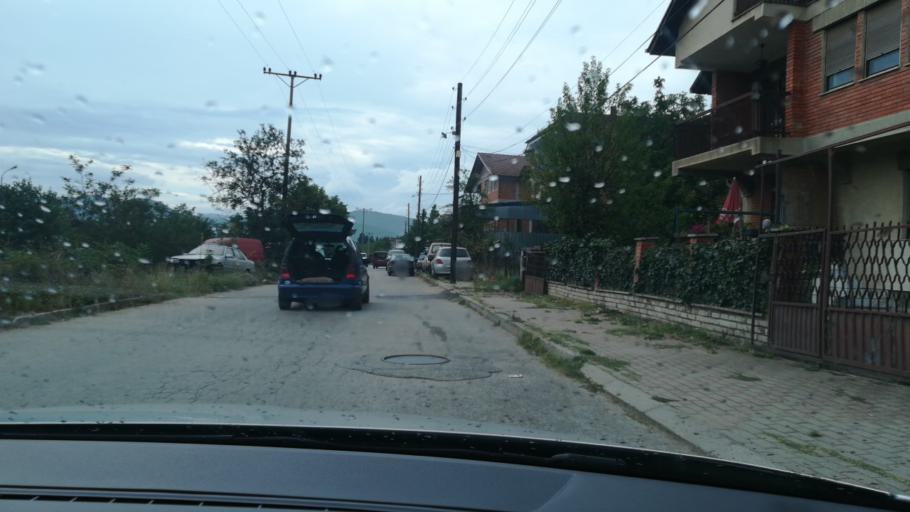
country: MK
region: Kicevo
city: Kicevo
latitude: 41.5129
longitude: 20.9494
